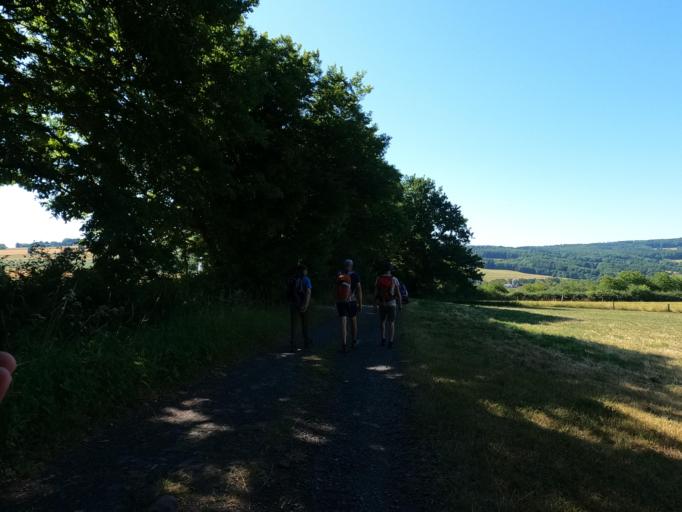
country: DE
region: Hesse
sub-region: Regierungsbezirk Darmstadt
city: Schluchtern
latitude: 50.3276
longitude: 9.5324
